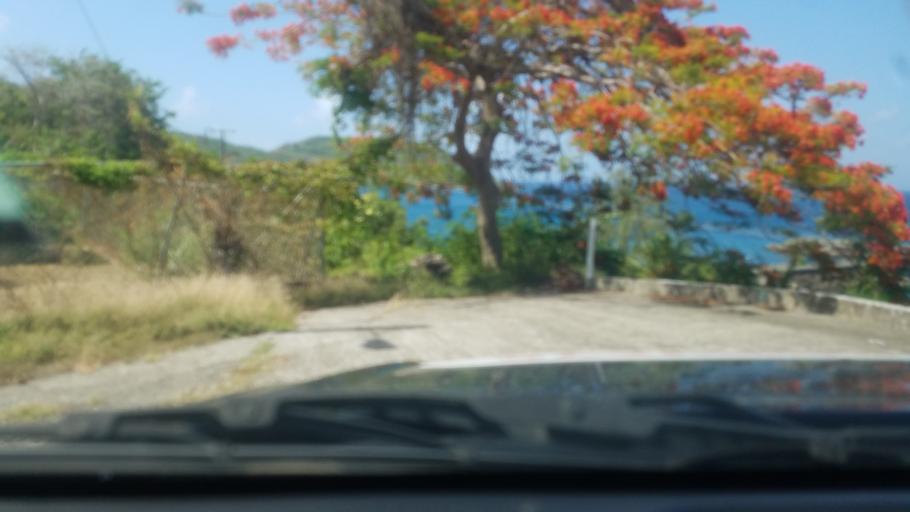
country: LC
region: Vieux-Fort
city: Vieux Fort
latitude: 13.7249
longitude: -60.9540
